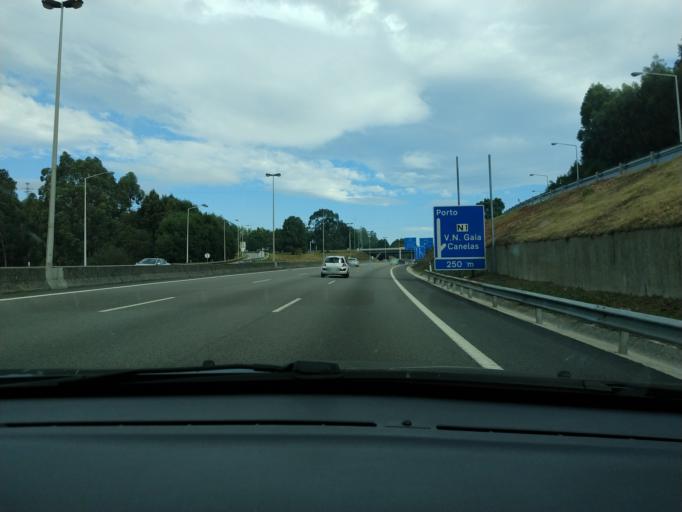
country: PT
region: Porto
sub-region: Vila Nova de Gaia
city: Perozinho
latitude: 41.0695
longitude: -8.5818
